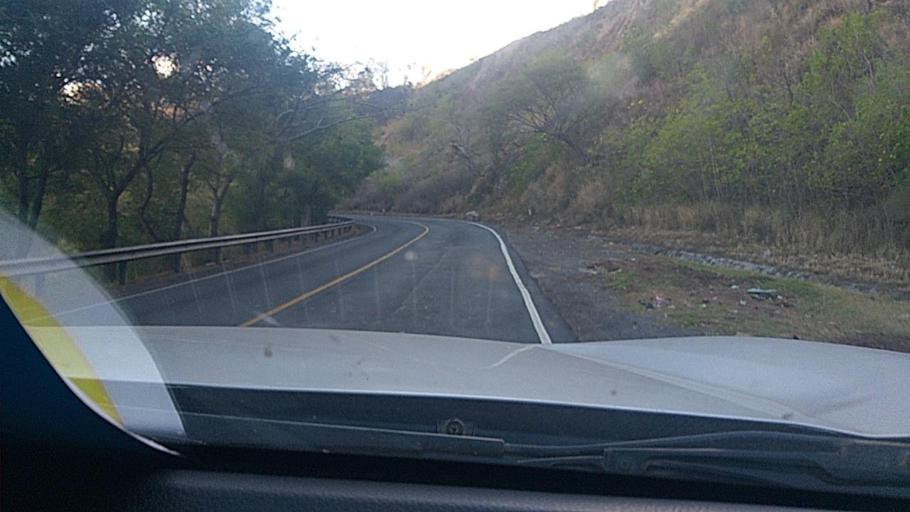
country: NI
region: Esteli
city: Condega
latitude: 13.2669
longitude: -86.3551
